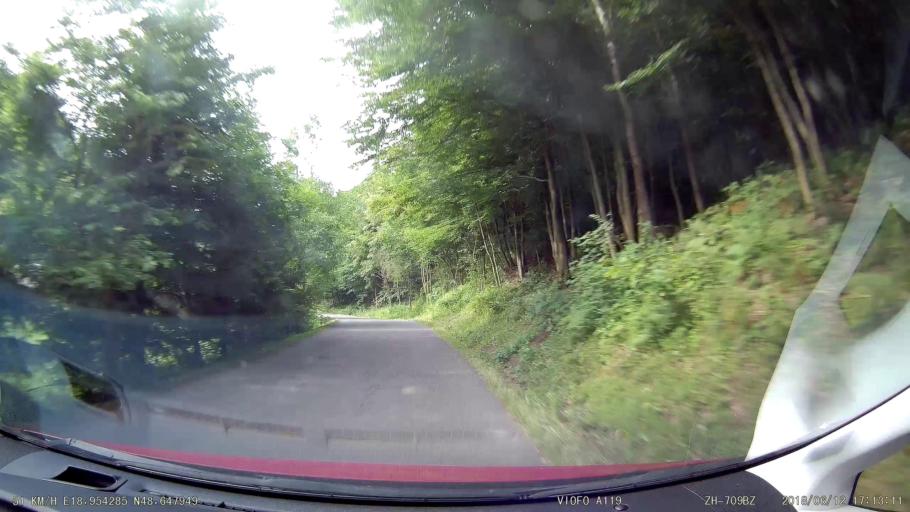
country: SK
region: Banskobystricky
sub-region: Okres Ziar nad Hronom
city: Kremnica
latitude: 48.6481
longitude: 18.9543
